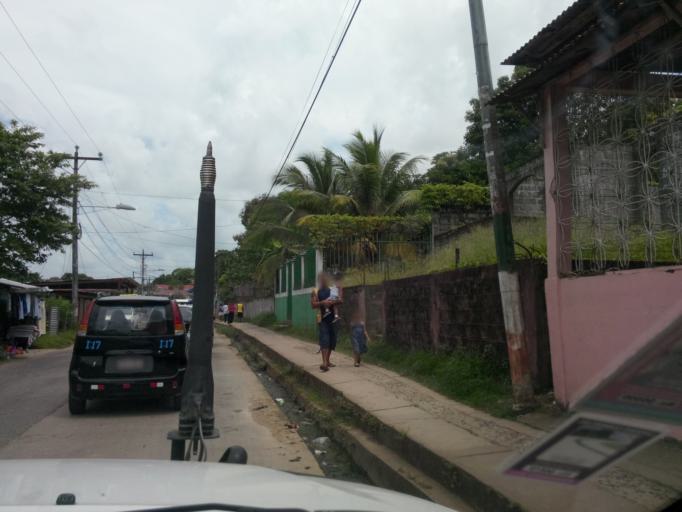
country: NI
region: Atlantico Sur
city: Bluefields
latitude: 12.0095
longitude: -83.7691
